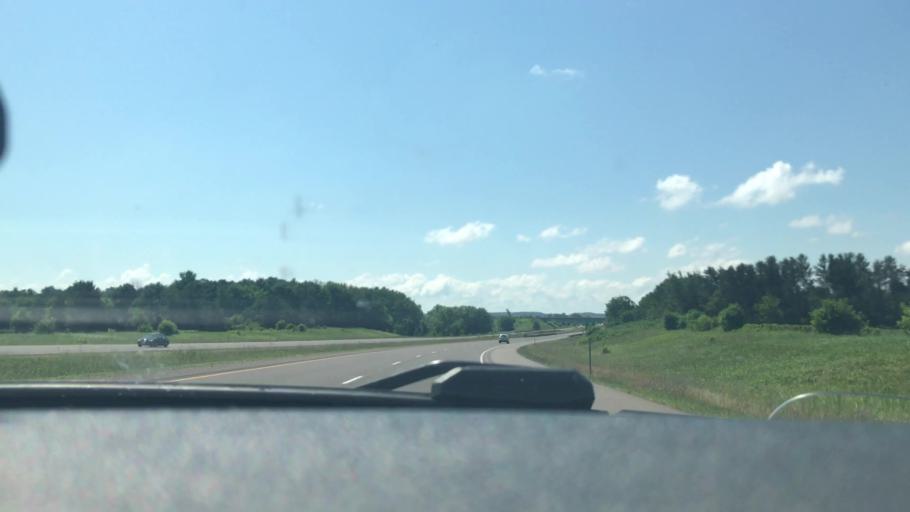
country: US
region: Wisconsin
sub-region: Chippewa County
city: Bloomer
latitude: 45.0219
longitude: -91.4436
